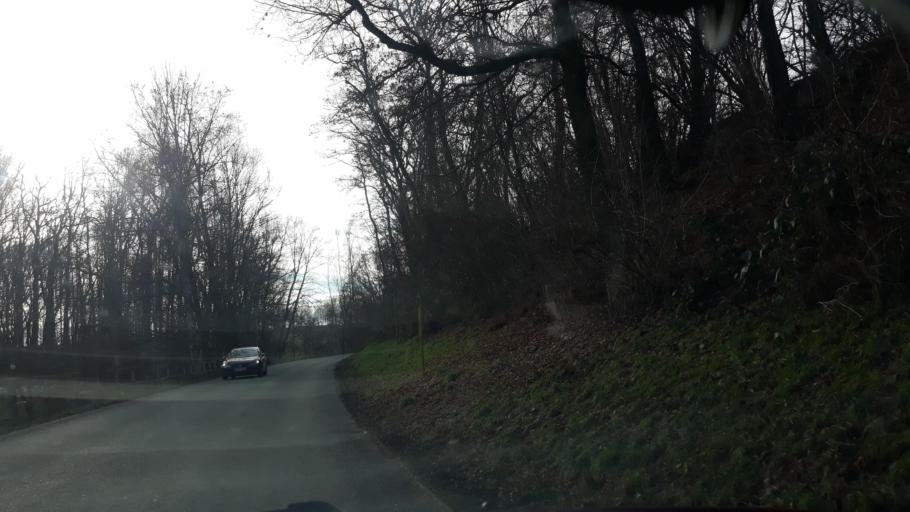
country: DE
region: Saxony
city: Mulsen
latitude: 50.7159
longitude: 12.5364
